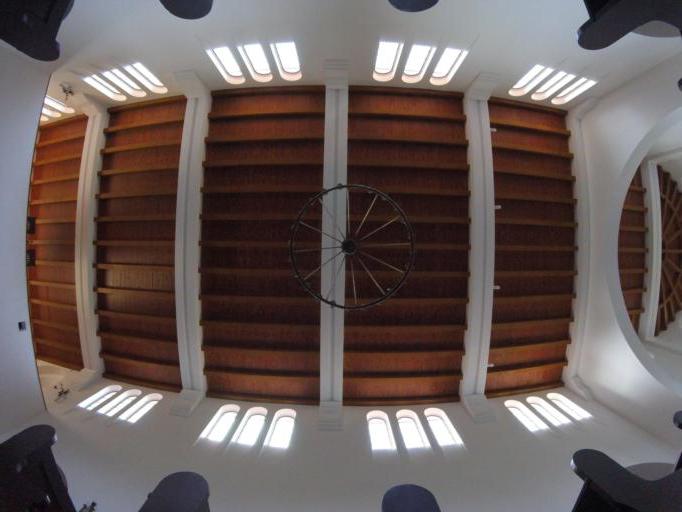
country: HU
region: Tolna
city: Bata
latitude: 46.1245
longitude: 18.7687
